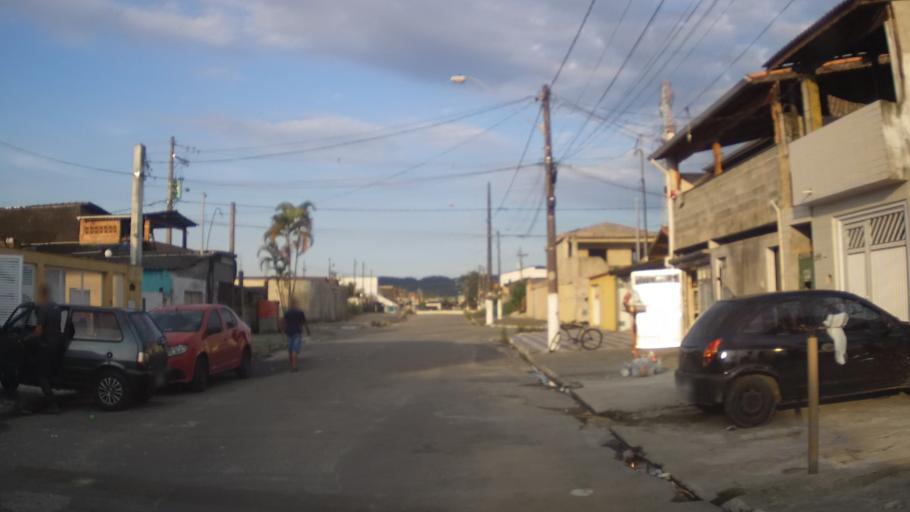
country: BR
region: Sao Paulo
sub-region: Praia Grande
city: Praia Grande
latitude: -23.9961
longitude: -46.4289
